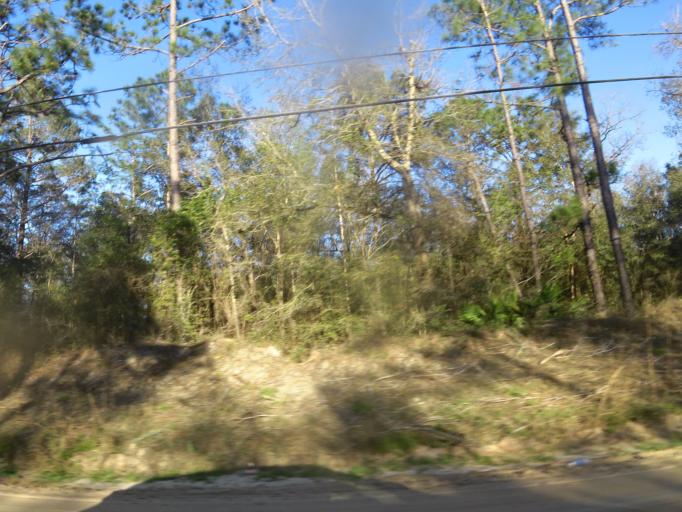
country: US
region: Florida
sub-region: Clay County
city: Middleburg
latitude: 30.1194
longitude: -81.8817
